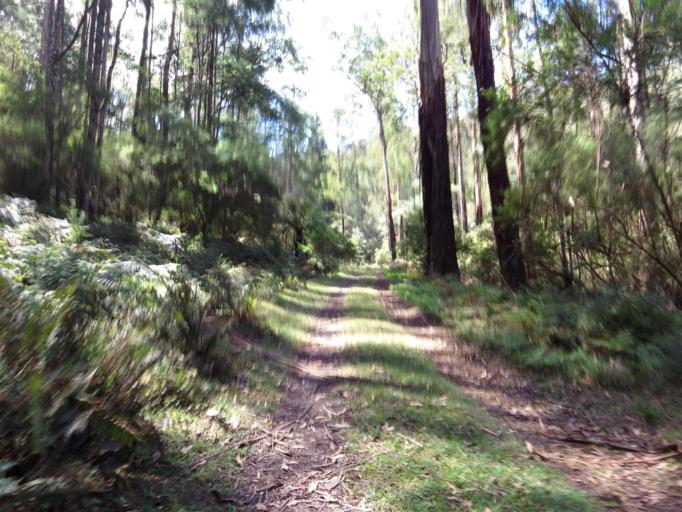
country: AU
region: Victoria
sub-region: Yarra Ranges
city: Millgrove
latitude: -37.6853
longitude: 145.8084
